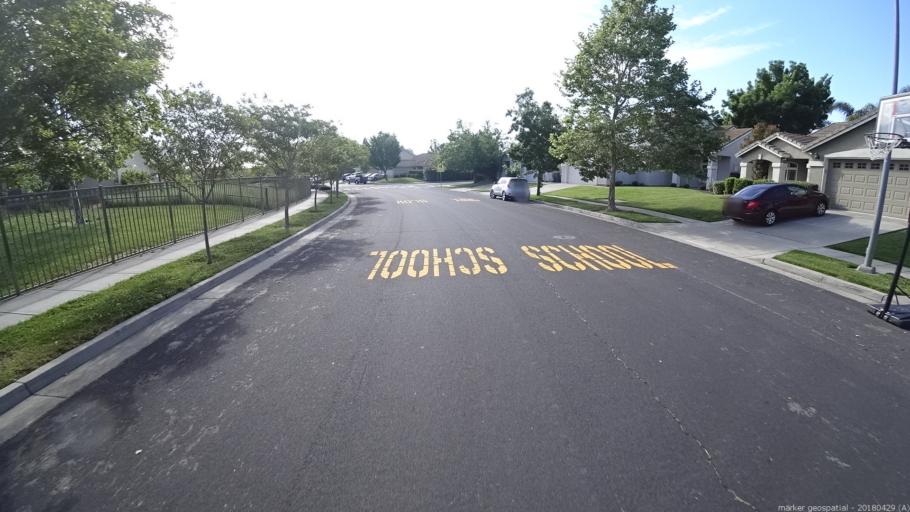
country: US
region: California
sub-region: Yolo County
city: West Sacramento
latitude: 38.5398
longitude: -121.5683
